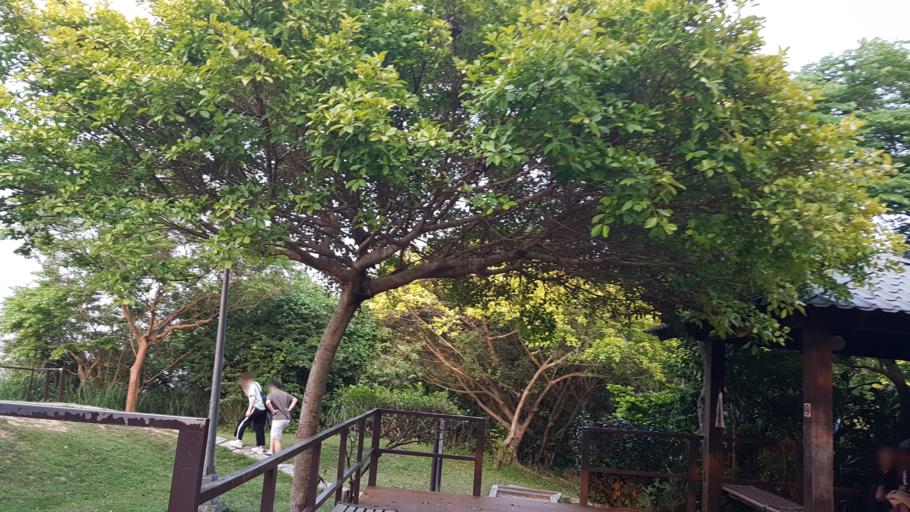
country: TW
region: Taipei
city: Taipei
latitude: 25.0167
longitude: 121.5537
